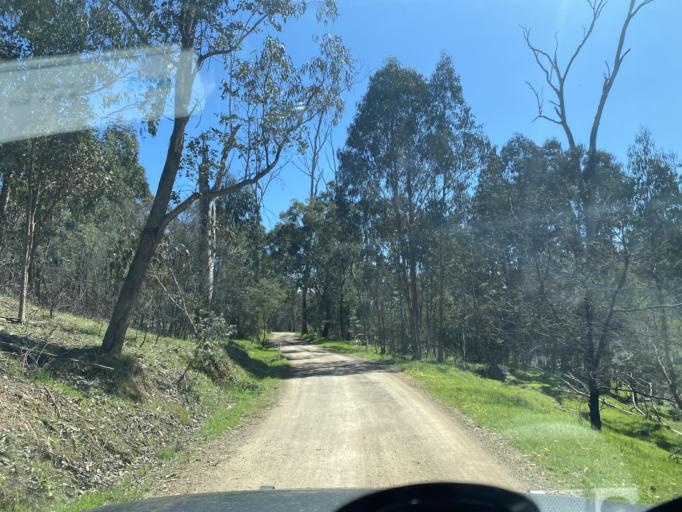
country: AU
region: Victoria
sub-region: Benalla
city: Benalla
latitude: -36.7086
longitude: 146.1787
